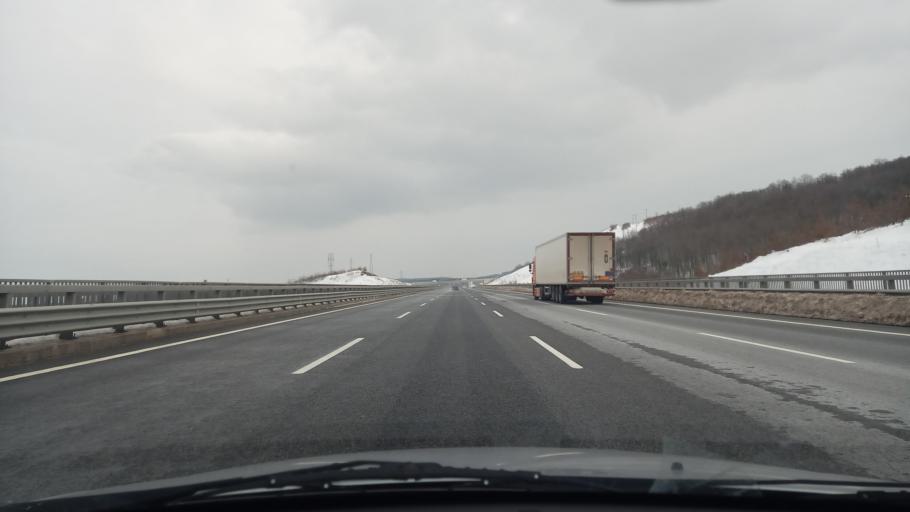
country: TR
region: Kocaeli
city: Derince
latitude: 40.8617
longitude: 29.8529
